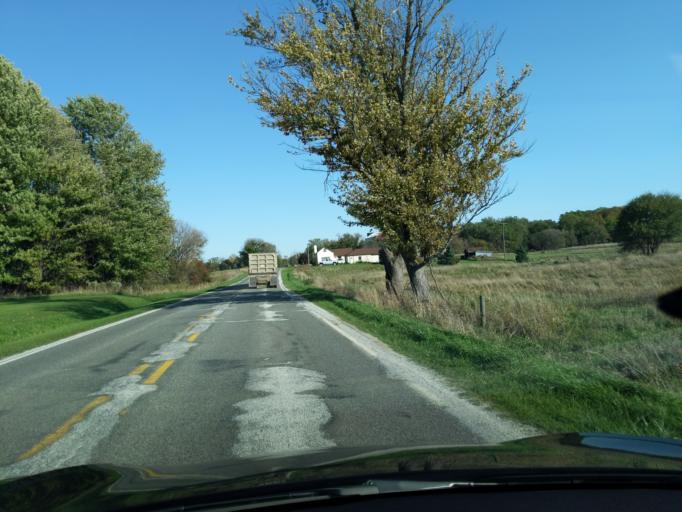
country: US
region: Michigan
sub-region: Clinton County
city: Saint Johns
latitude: 42.9309
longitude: -84.4977
